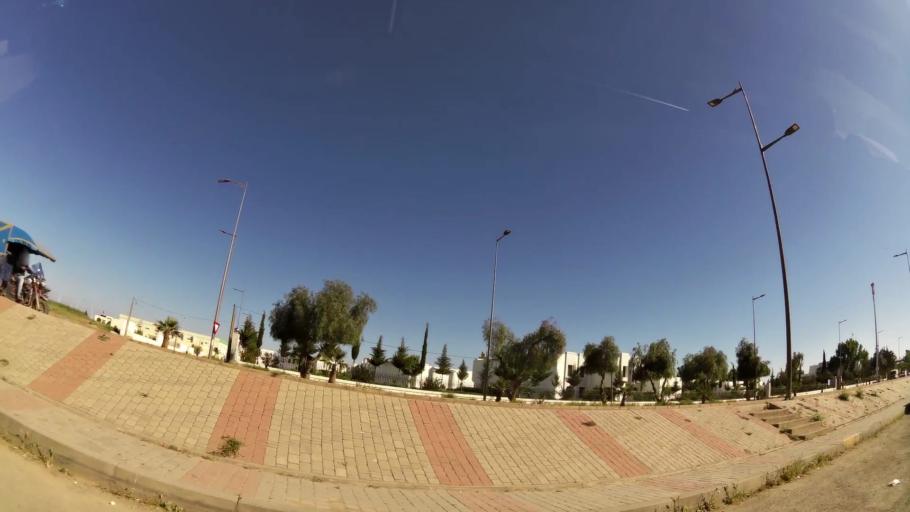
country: MA
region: Fes-Boulemane
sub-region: Fes
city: Fes
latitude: 34.0086
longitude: -4.9630
